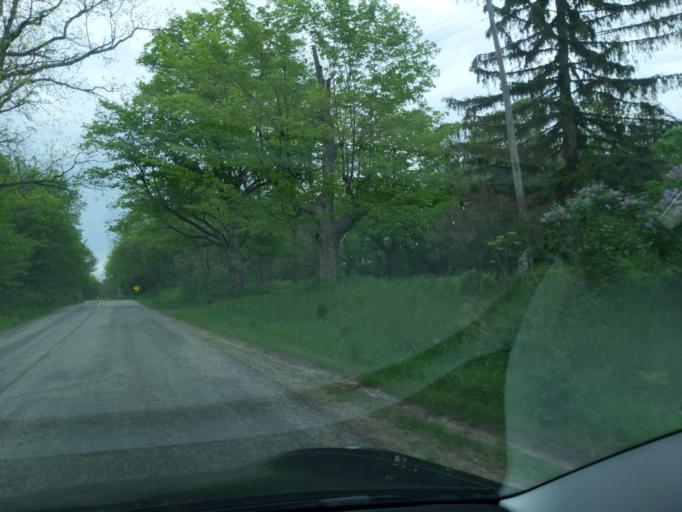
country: US
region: Michigan
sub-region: Ingham County
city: Stockbridge
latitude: 42.5133
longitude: -84.2822
